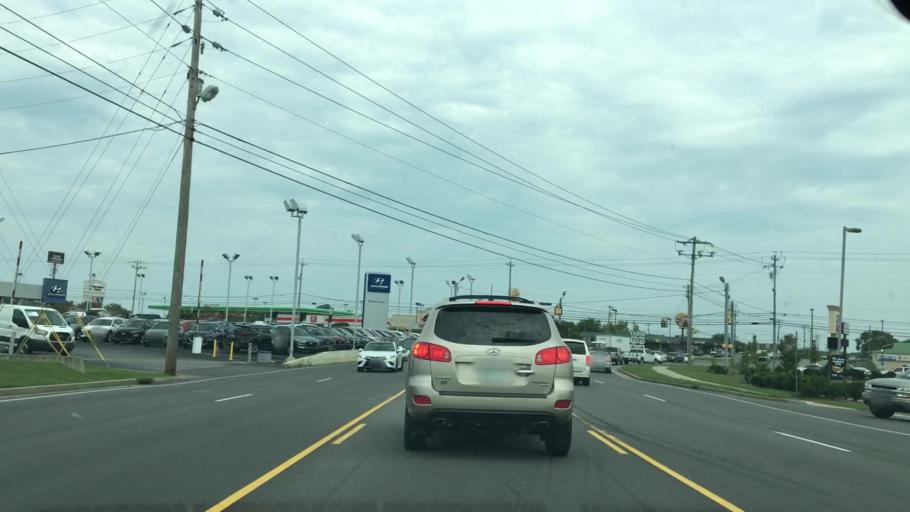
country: US
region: Tennessee
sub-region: Wilson County
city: Lebanon
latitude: 36.2123
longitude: -86.3221
